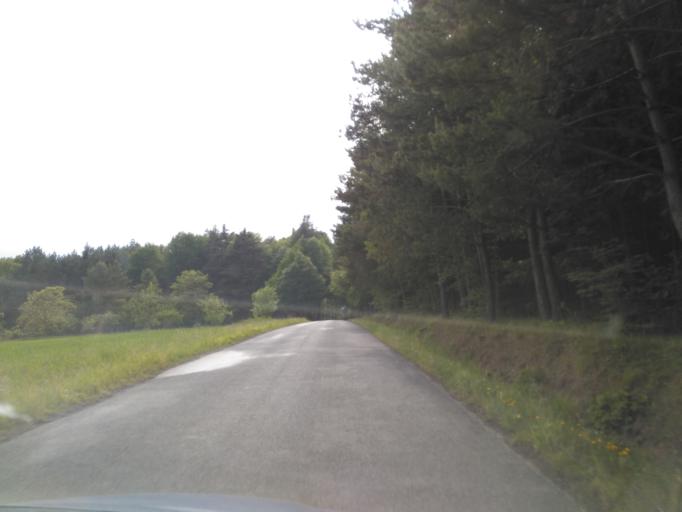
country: CZ
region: Central Bohemia
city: Hudlice
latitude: 49.9607
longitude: 13.9484
